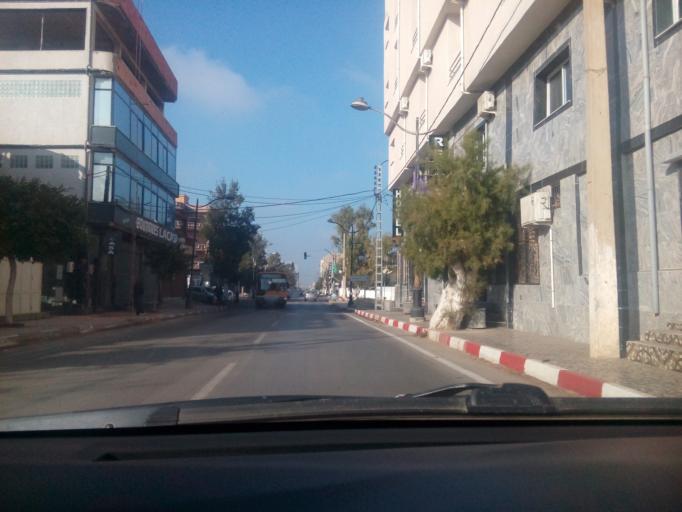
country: DZ
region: Oran
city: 'Ain el Turk
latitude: 35.7357
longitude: -0.7417
